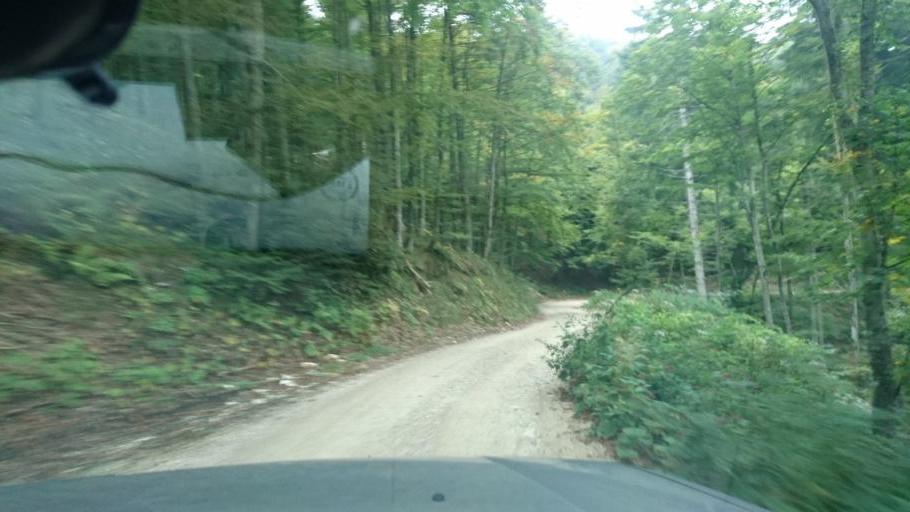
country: IT
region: Veneto
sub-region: Provincia di Vicenza
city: Enego
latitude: 45.9400
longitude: 11.6716
